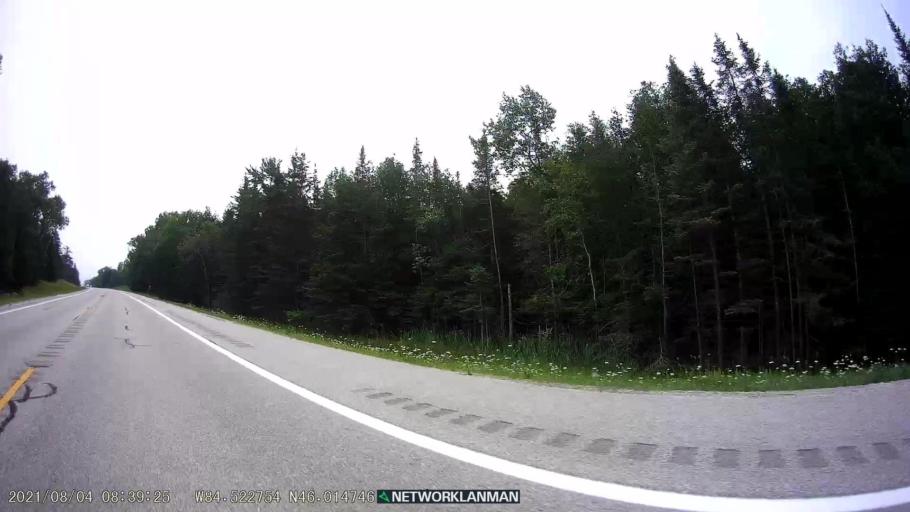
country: US
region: Michigan
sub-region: Mackinac County
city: Saint Ignace
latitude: 46.0145
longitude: -84.5202
